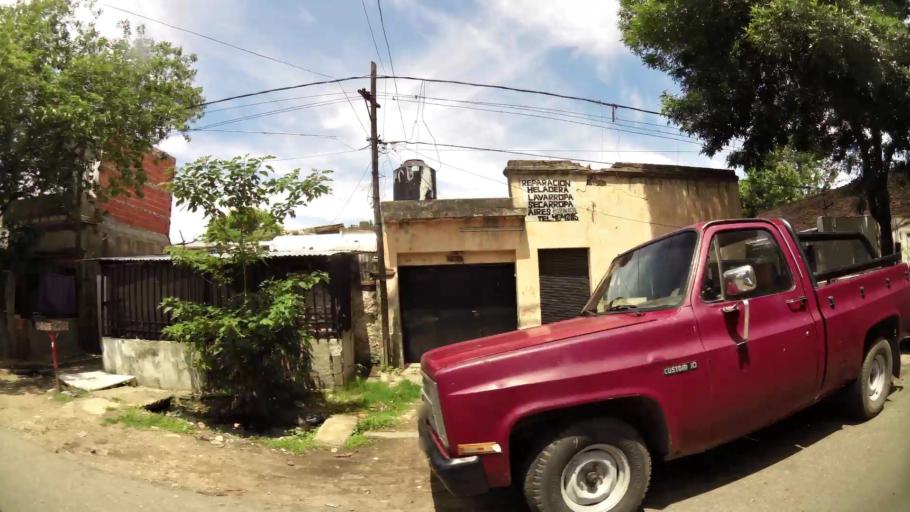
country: AR
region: Santa Fe
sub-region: Departamento de Rosario
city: Rosario
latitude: -32.9835
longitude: -60.6353
